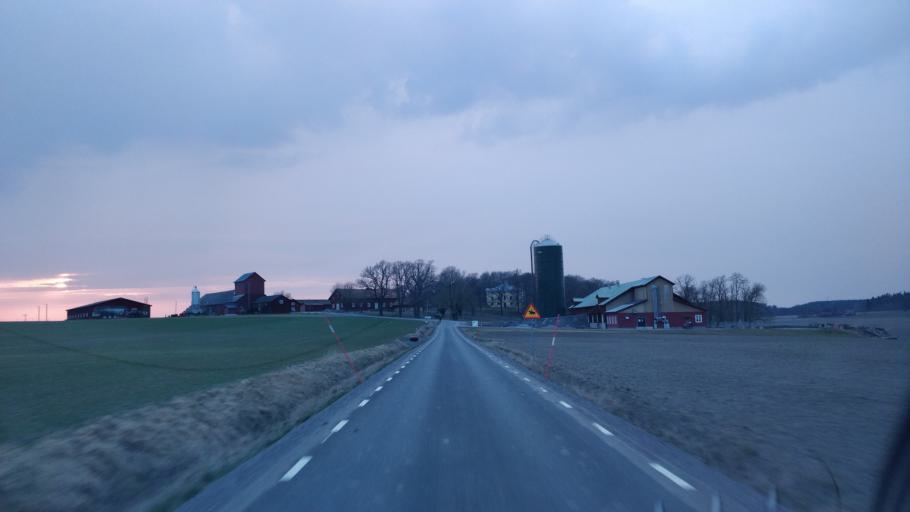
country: SE
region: Uppsala
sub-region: Enkopings Kommun
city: Orsundsbro
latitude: 59.7386
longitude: 17.1855
